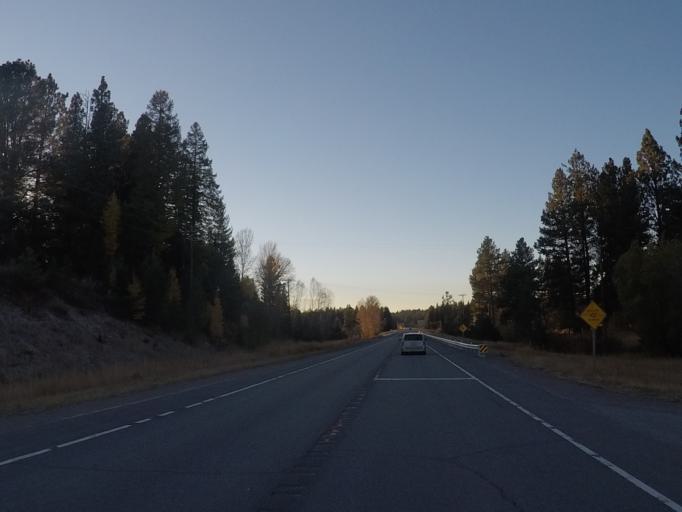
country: US
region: Montana
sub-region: Lewis and Clark County
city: Lincoln
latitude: 46.9988
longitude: -113.0334
